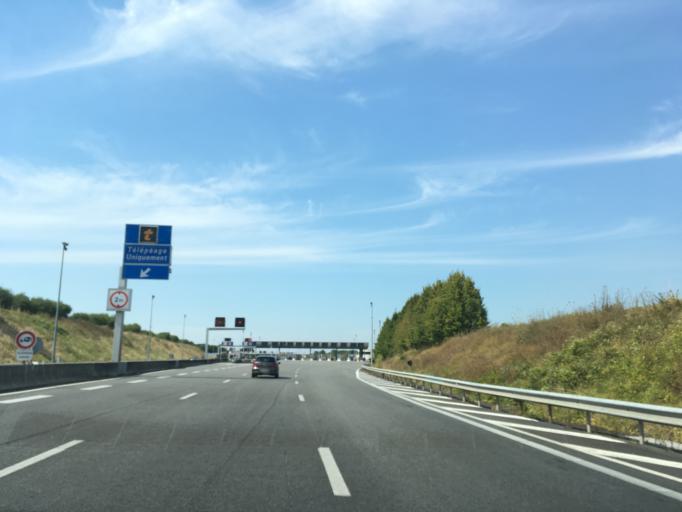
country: FR
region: Ile-de-France
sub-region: Departement des Yvelines
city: Carrieres-sur-Seine
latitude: 48.9130
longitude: 2.1661
